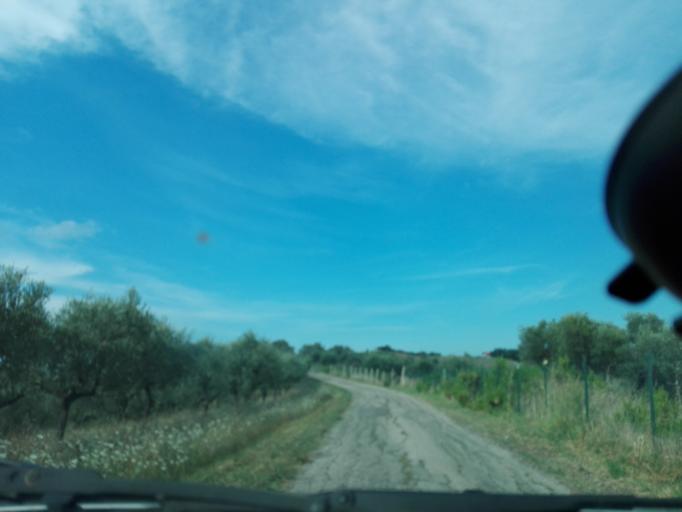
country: IT
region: Abruzzo
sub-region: Provincia di Pescara
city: Cappelle sul Tavo
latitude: 42.4531
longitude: 14.1076
